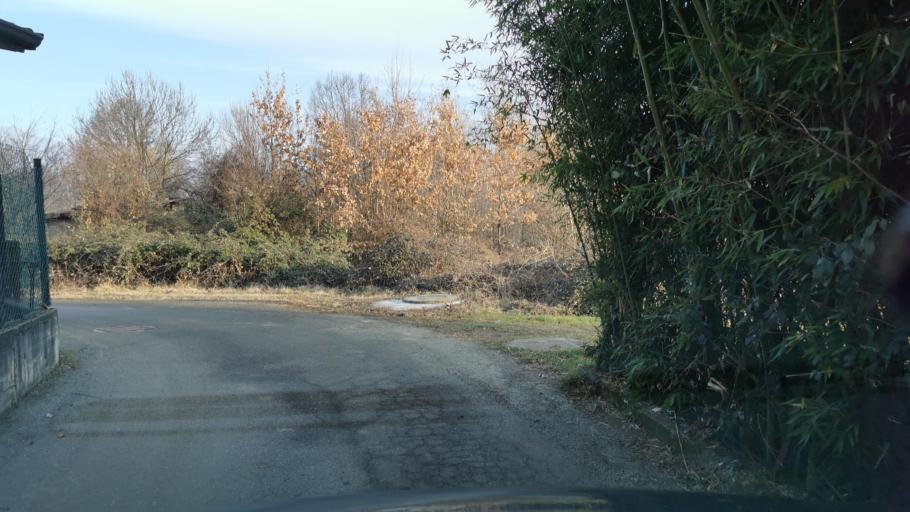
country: IT
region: Piedmont
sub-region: Provincia di Torino
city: Rocca Canavese
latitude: 45.2845
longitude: 7.5760
